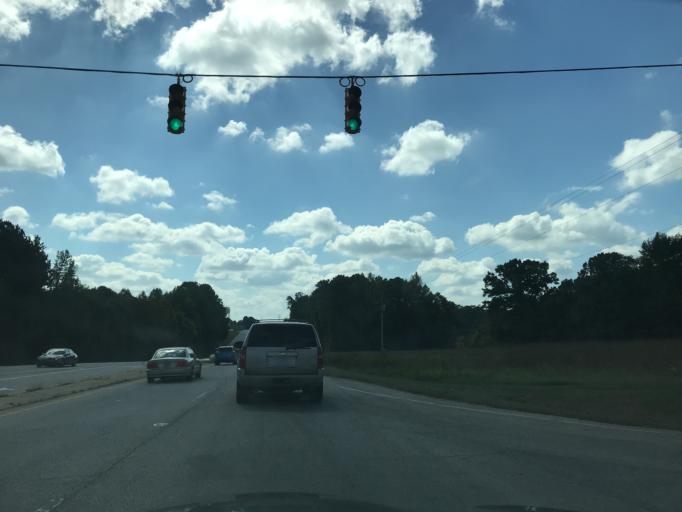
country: US
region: North Carolina
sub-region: Franklin County
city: Youngsville
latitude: 36.0594
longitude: -78.4861
